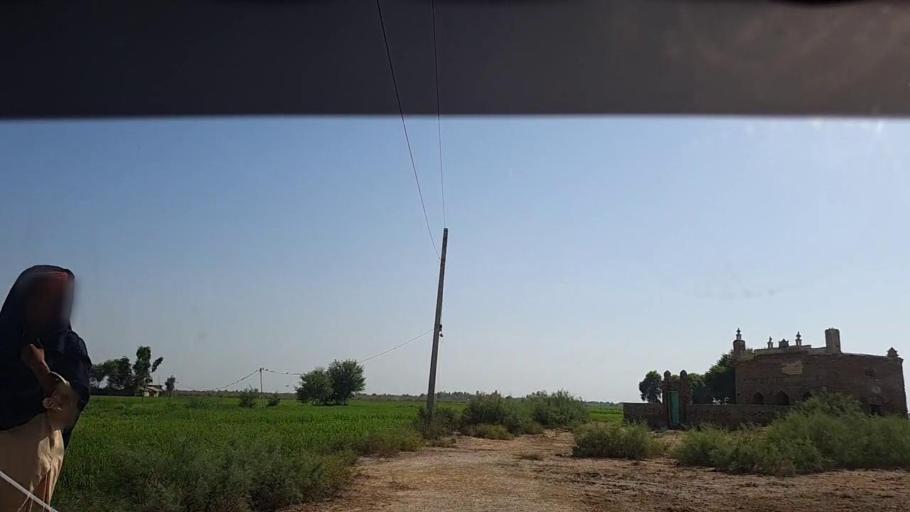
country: PK
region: Sindh
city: Ghauspur
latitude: 28.1780
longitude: 69.0284
